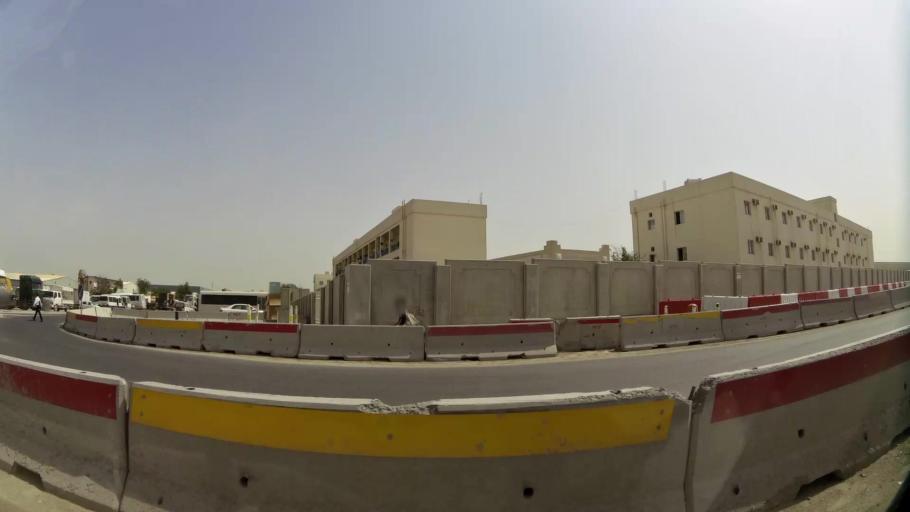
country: QA
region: Baladiyat ar Rayyan
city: Ar Rayyan
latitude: 25.1937
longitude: 51.4180
